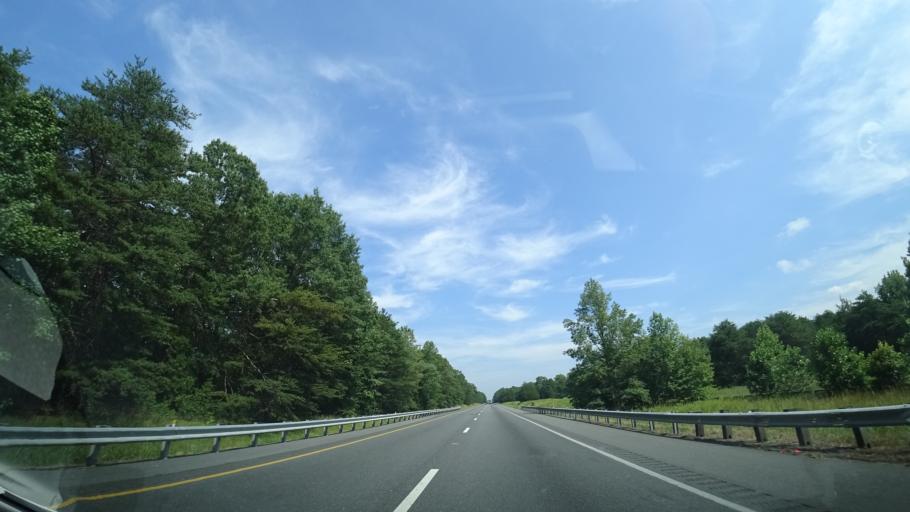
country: US
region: Virginia
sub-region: Louisa County
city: Louisa
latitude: 37.9125
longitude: -78.0672
